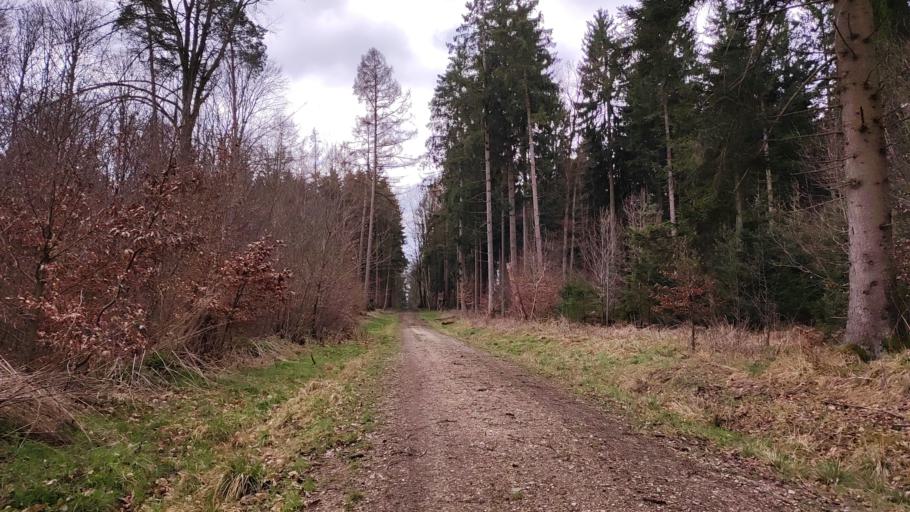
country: DE
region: Bavaria
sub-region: Swabia
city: Landensberg
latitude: 48.4316
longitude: 10.5566
